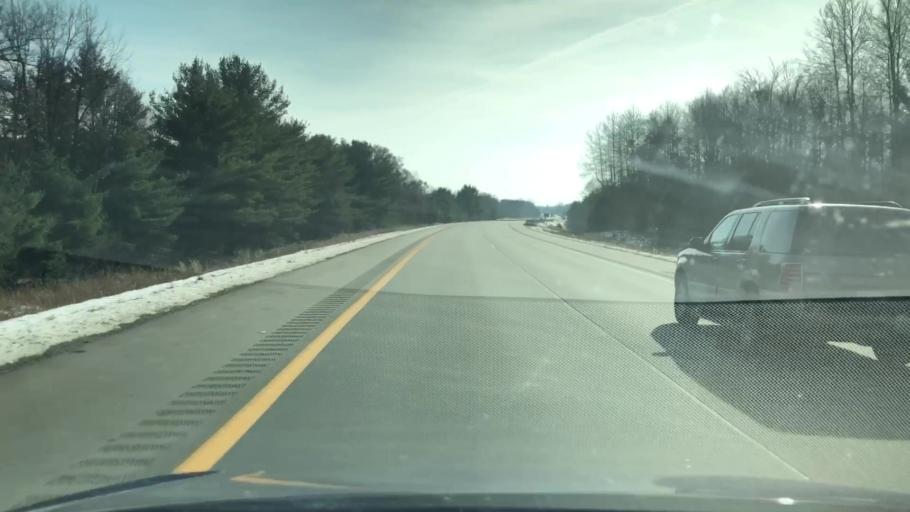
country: US
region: Michigan
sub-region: Ogemaw County
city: Skidway Lake
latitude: 44.1206
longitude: -84.1222
